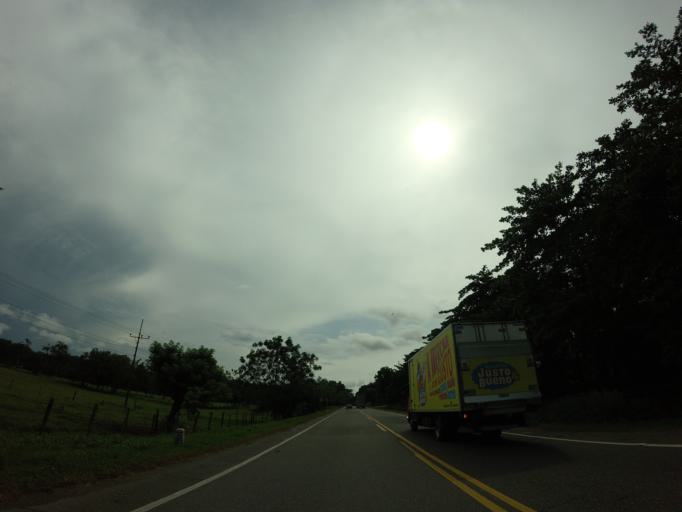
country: CO
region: Caldas
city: La Dorada
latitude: 5.4047
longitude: -74.6933
